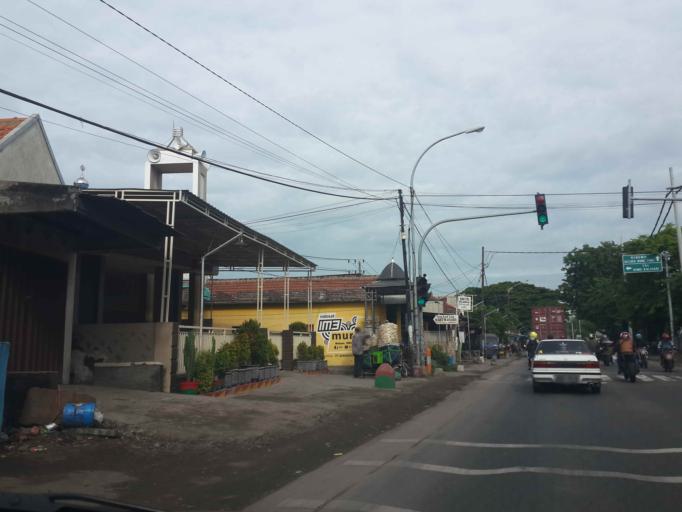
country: ID
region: East Java
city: Kebomas
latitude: -7.1979
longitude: 112.6472
